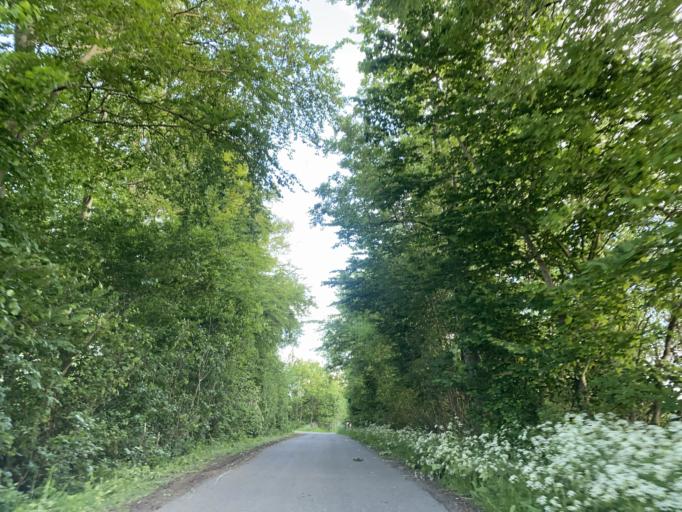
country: DK
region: Central Jutland
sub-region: Viborg Kommune
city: Bjerringbro
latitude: 56.3255
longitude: 9.6609
